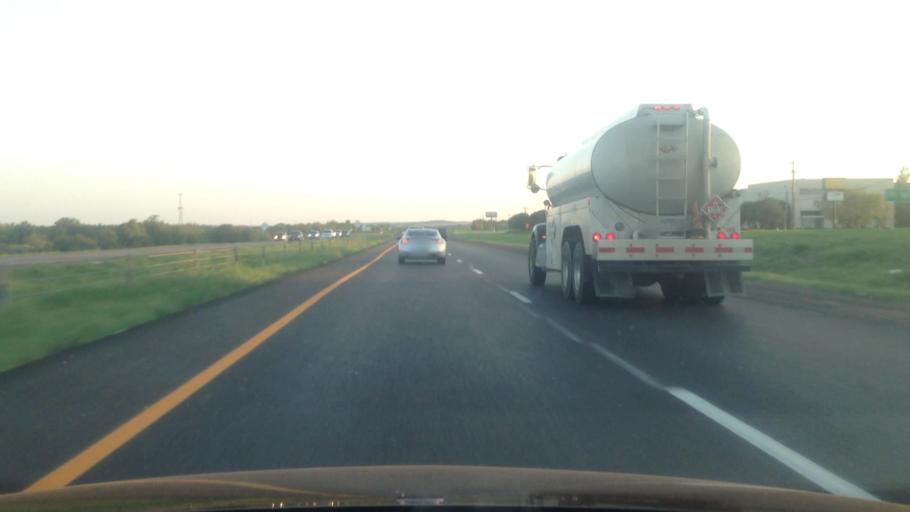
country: US
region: Texas
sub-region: Denton County
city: Denton
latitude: 33.1963
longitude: -97.1673
